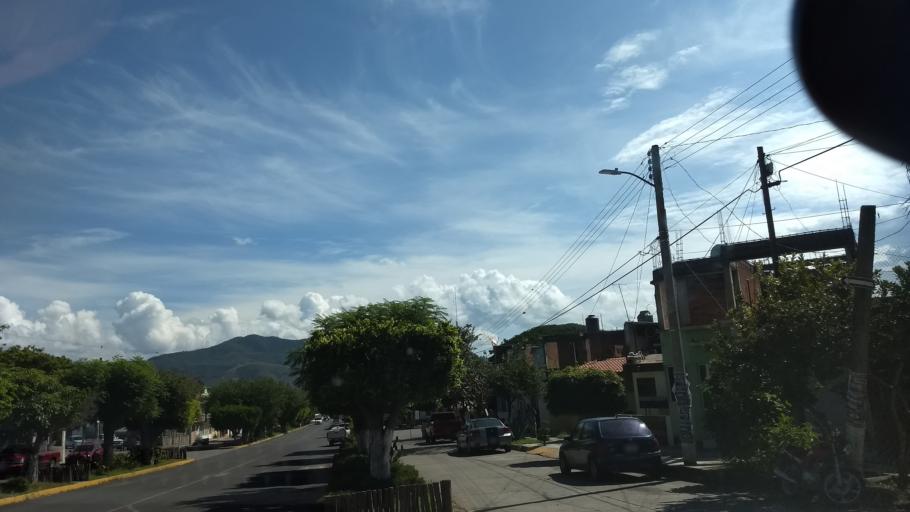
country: MX
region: Jalisco
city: Tuxpan
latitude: 19.5577
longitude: -103.3882
